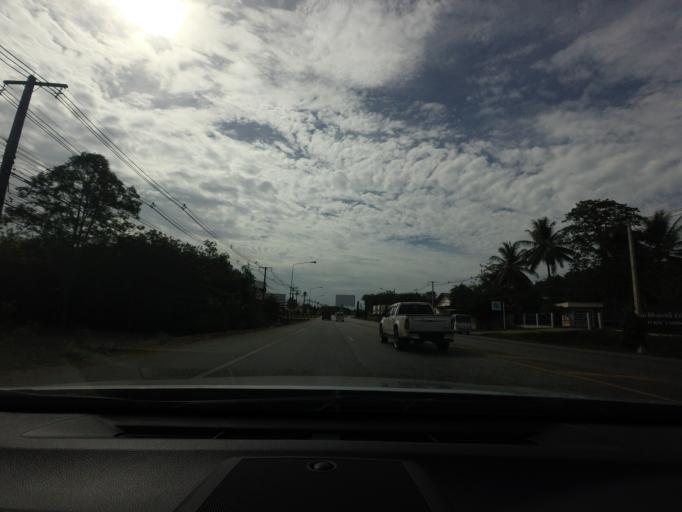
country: TH
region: Songkhla
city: Hat Yai
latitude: 6.9764
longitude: 100.4273
